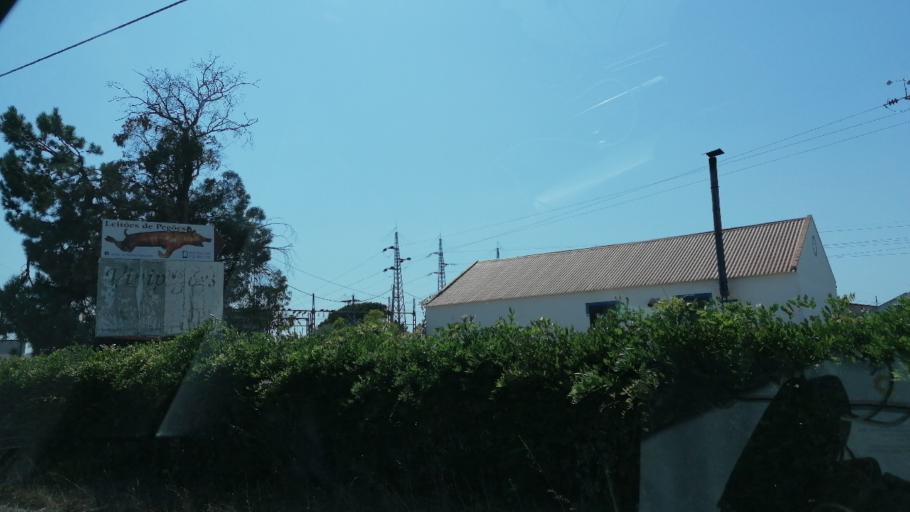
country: PT
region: Evora
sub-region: Vendas Novas
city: Vendas Novas
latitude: 38.6900
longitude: -8.6126
